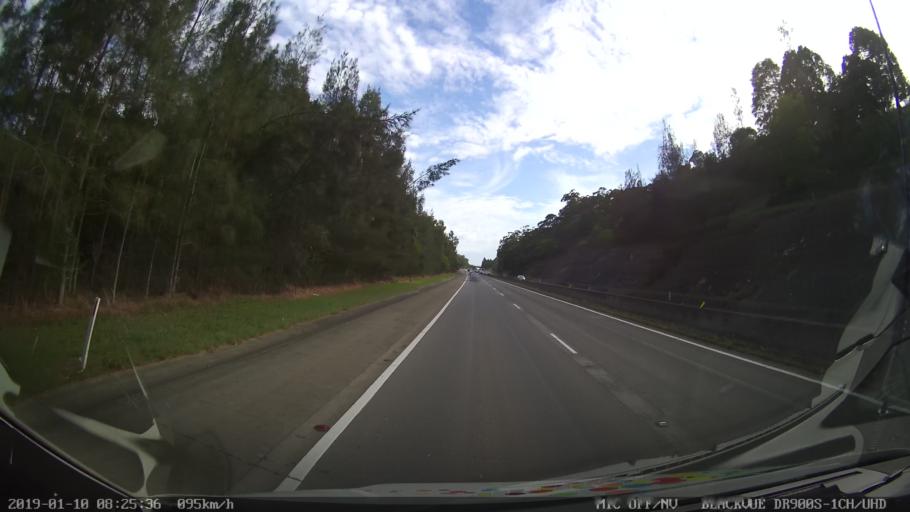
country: AU
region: New South Wales
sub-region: Coffs Harbour
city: Bonville
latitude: -30.4317
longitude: 153.0180
